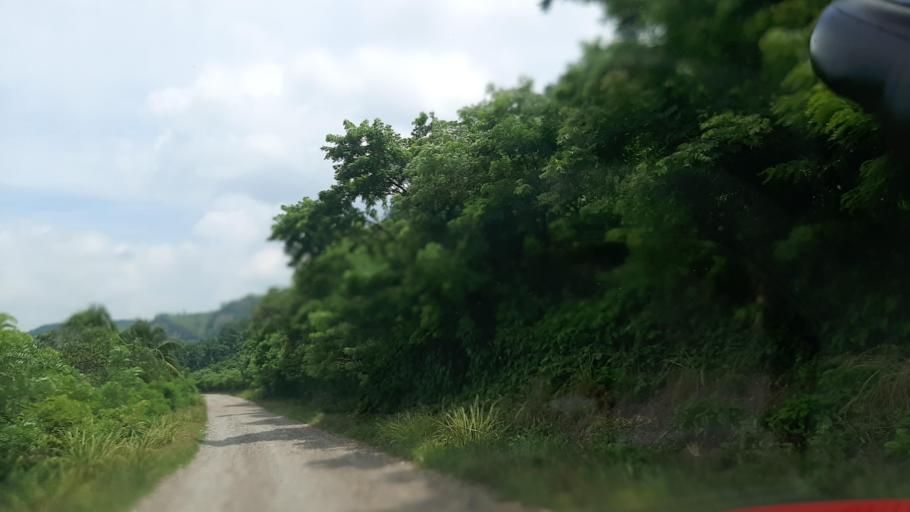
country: MX
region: Veracruz
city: Gutierrez Zamora
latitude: 20.4585
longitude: -97.1812
